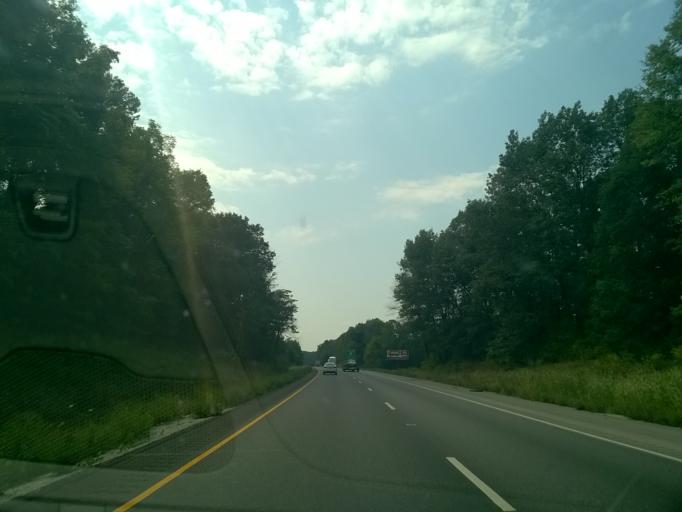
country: US
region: Indiana
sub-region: Clay County
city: Brazil
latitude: 39.4534
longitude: -87.1030
